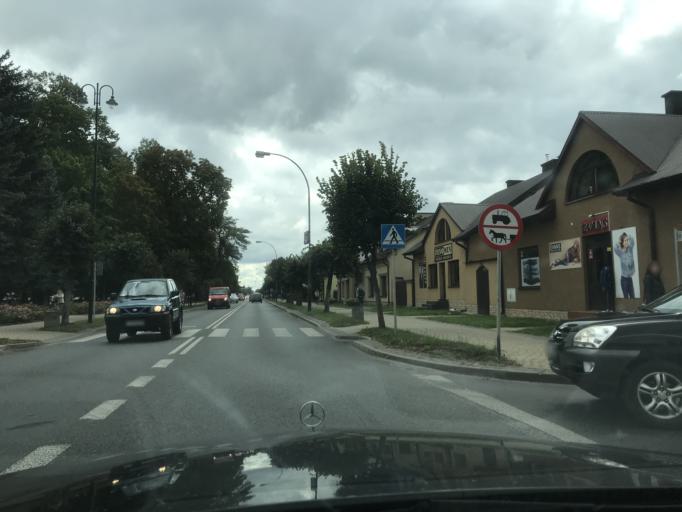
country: PL
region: Lublin Voivodeship
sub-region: Powiat janowski
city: Janow Lubelski
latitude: 50.7047
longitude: 22.4141
